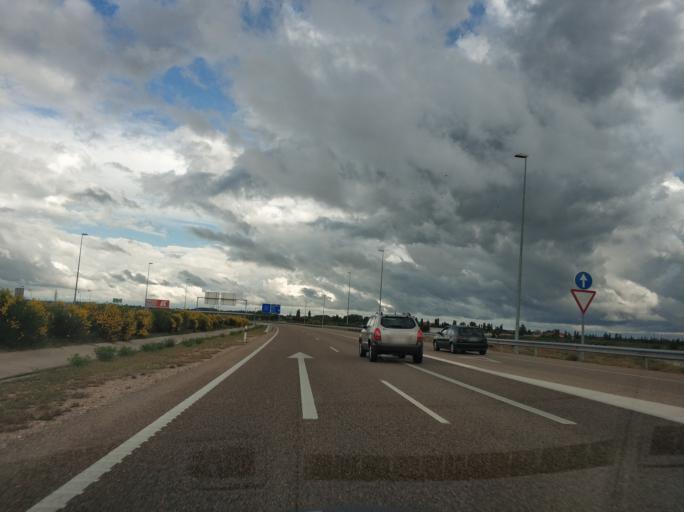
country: ES
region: Castille and Leon
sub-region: Provincia de Valladolid
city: Arroyo
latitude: 41.6116
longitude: -4.7714
